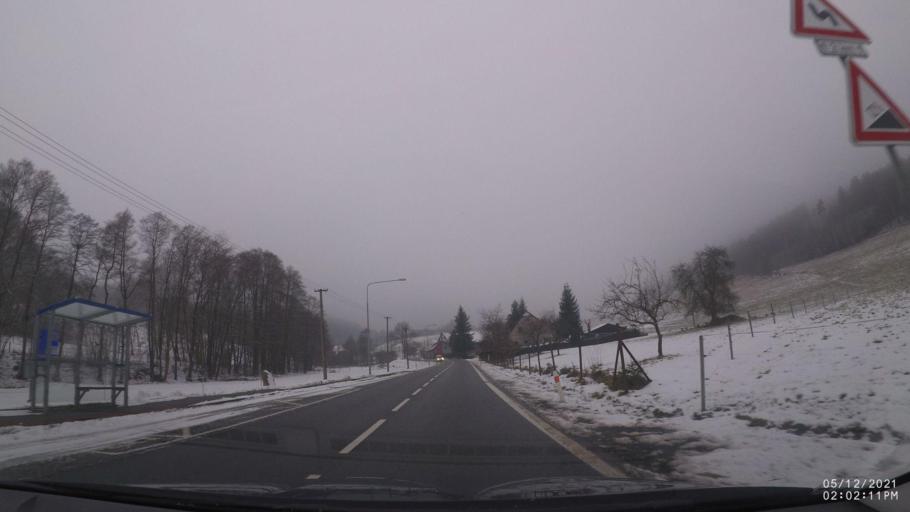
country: CZ
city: Hronov
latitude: 50.4843
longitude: 16.1470
